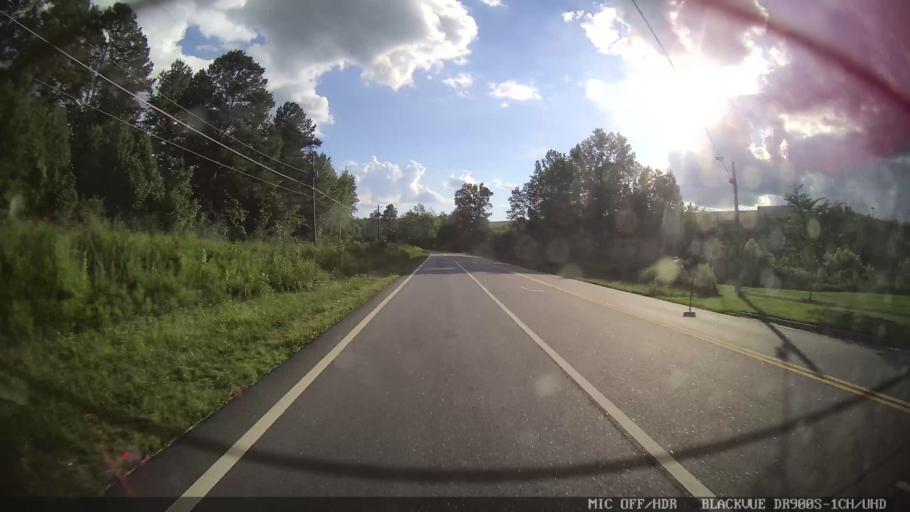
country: US
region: Georgia
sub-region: Bartow County
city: Cartersville
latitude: 34.2684
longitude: -84.8268
